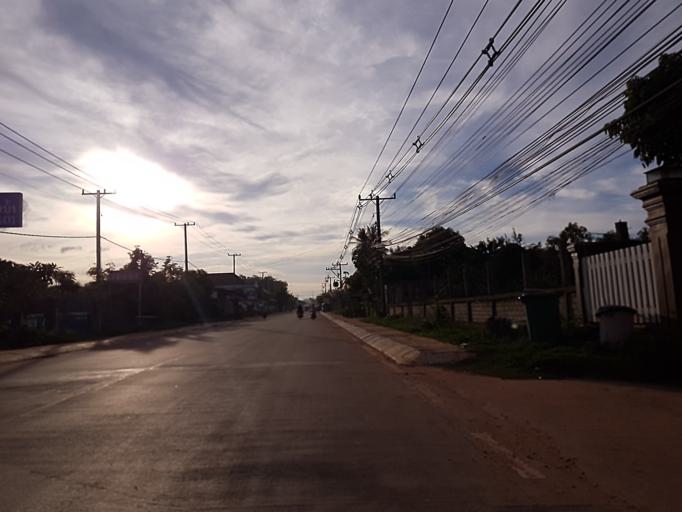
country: TH
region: Nong Khai
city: Si Chiang Mai
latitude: 18.0182
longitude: 102.5383
